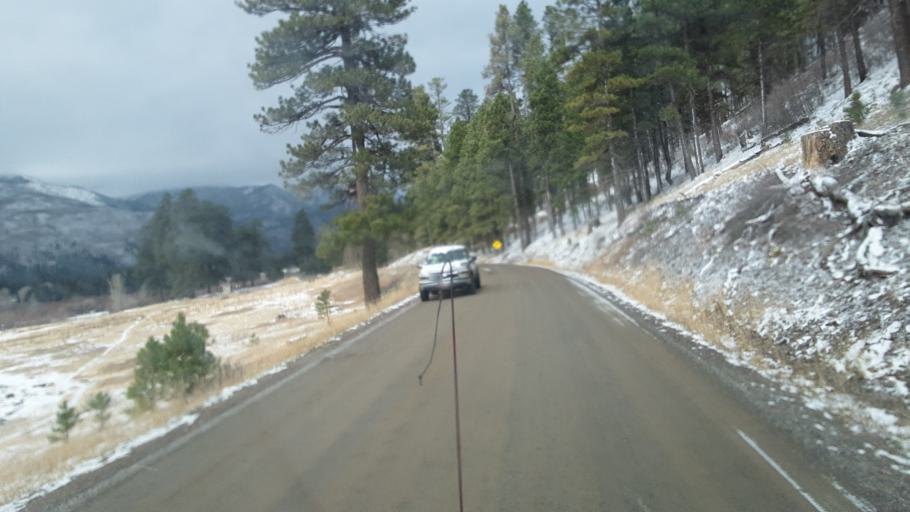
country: US
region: Colorado
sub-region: La Plata County
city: Bayfield
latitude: 37.4304
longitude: -107.5409
